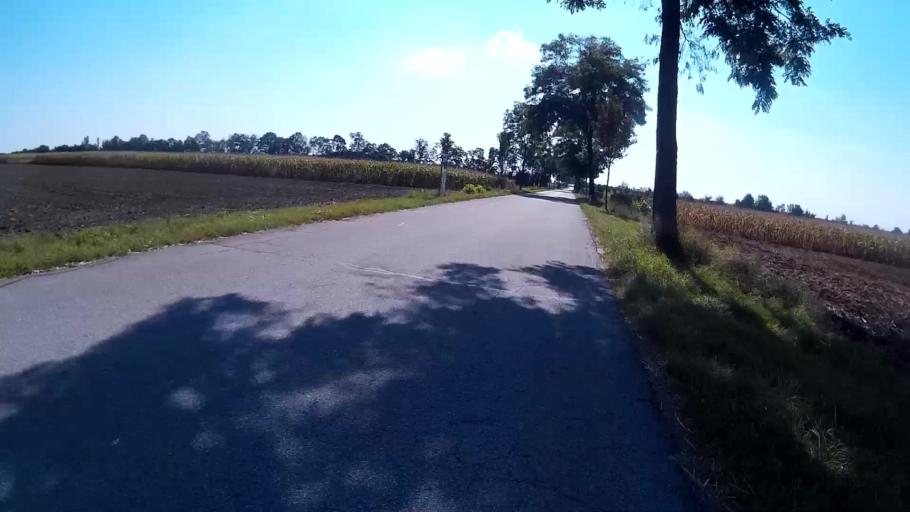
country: CZ
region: South Moravian
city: Novosedly
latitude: 48.7843
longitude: 16.4918
